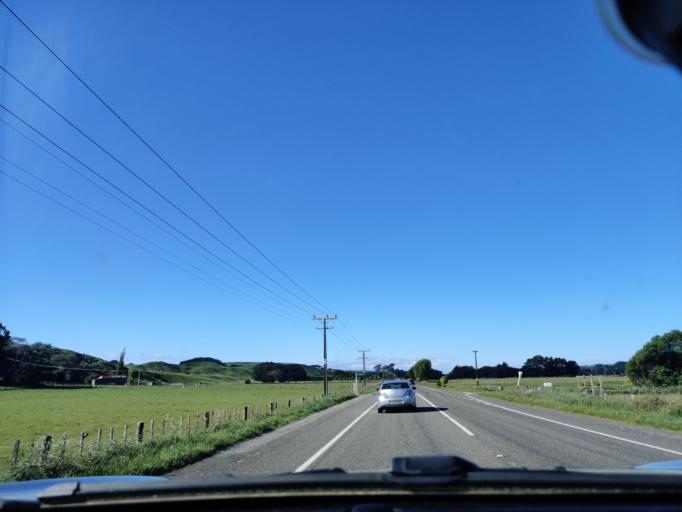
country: NZ
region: Manawatu-Wanganui
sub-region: Palmerston North City
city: Palmerston North
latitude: -40.6003
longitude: 175.7140
